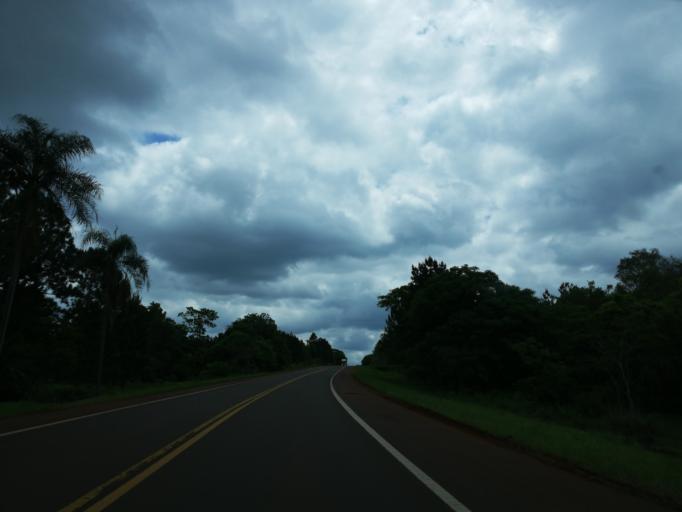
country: AR
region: Misiones
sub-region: Departamento de Leandro N. Alem
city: Leandro N. Alem
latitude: -27.6472
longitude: -55.3593
